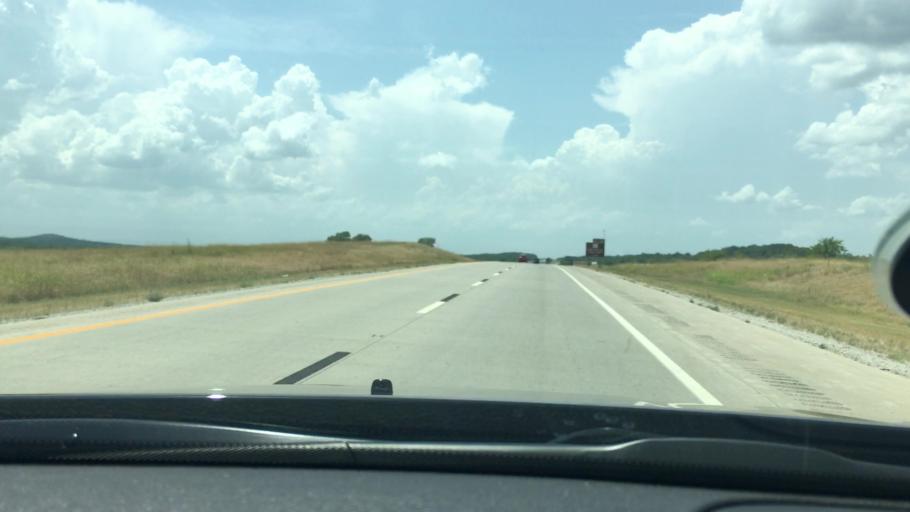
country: US
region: Oklahoma
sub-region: Carter County
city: Ardmore
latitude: 34.0874
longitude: -97.1513
